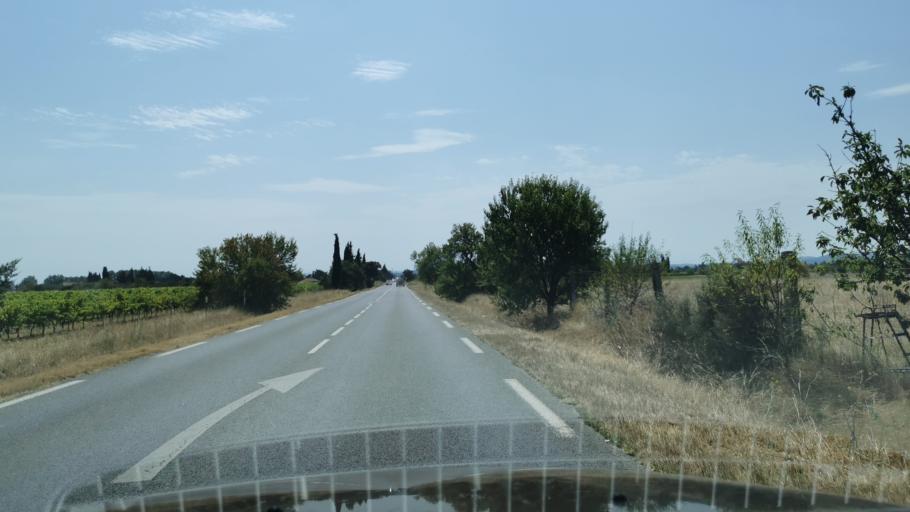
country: FR
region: Languedoc-Roussillon
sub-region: Departement de l'Aude
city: Ginestas
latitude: 43.2710
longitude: 2.8926
